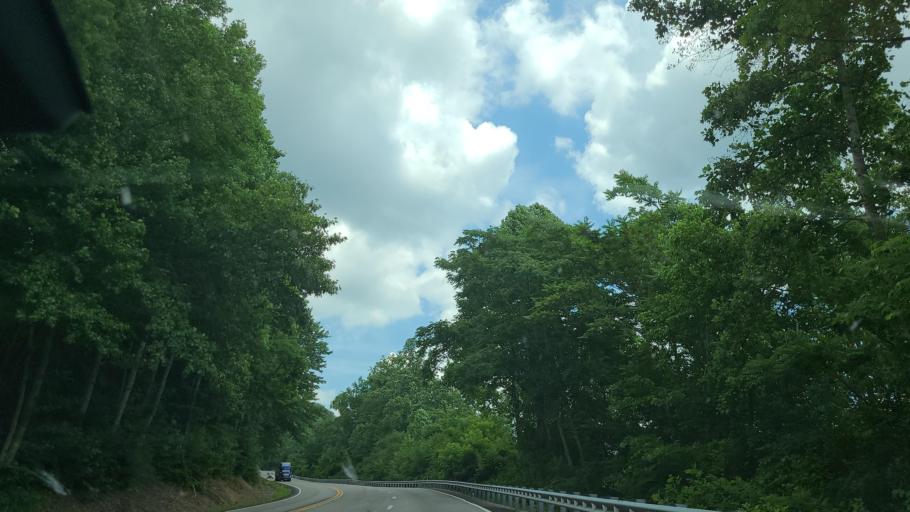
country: US
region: Tennessee
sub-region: Cumberland County
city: Lake Tansi
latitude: 35.7617
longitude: -85.0518
